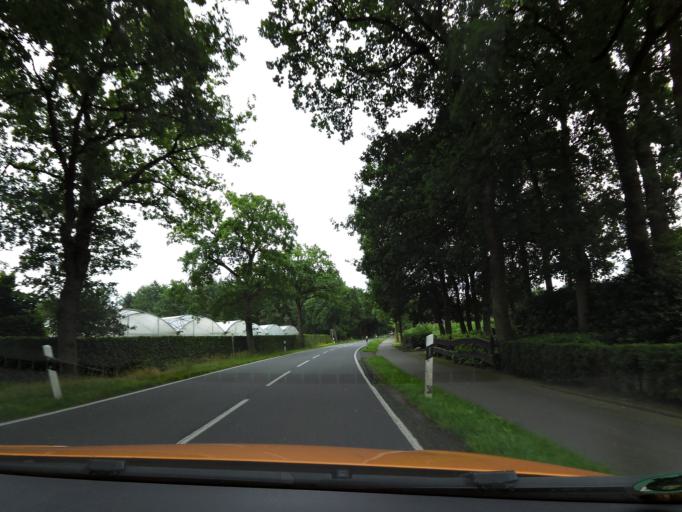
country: DE
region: Lower Saxony
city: Wiefelstede
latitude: 53.2060
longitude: 8.1151
